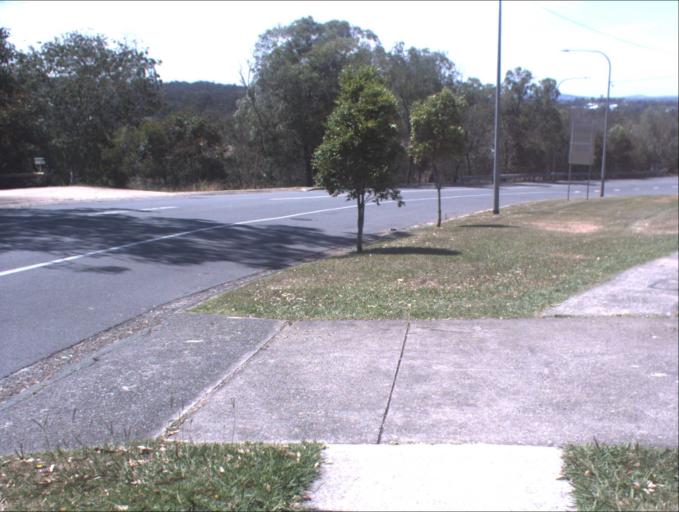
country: AU
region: Queensland
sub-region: Logan
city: Slacks Creek
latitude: -27.6313
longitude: 153.1550
